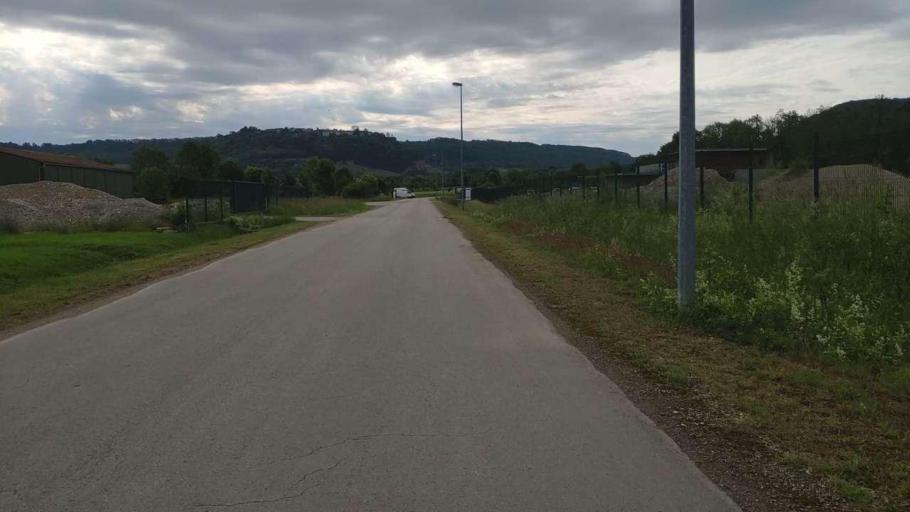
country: FR
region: Franche-Comte
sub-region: Departement du Jura
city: Perrigny
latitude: 46.7578
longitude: 5.5972
